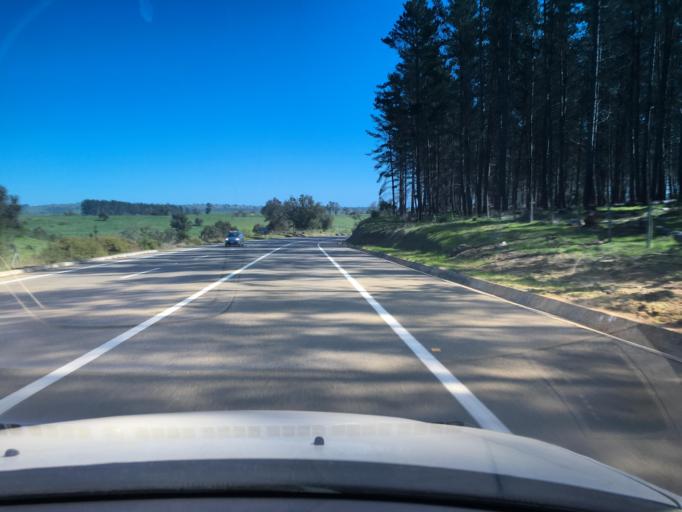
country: CL
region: Valparaiso
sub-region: San Antonio Province
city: El Tabo
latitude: -33.4091
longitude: -71.5119
